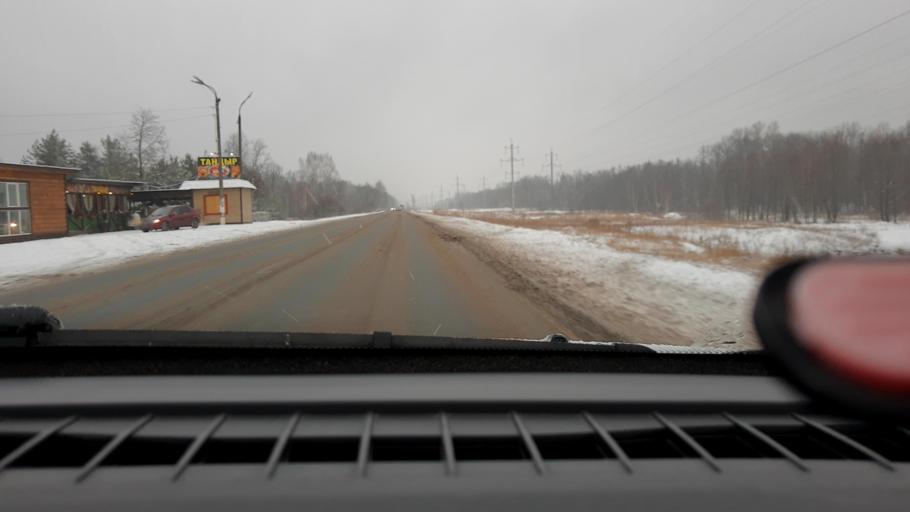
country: RU
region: Nizjnij Novgorod
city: Novaya Balakhna
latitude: 56.4686
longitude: 43.6152
